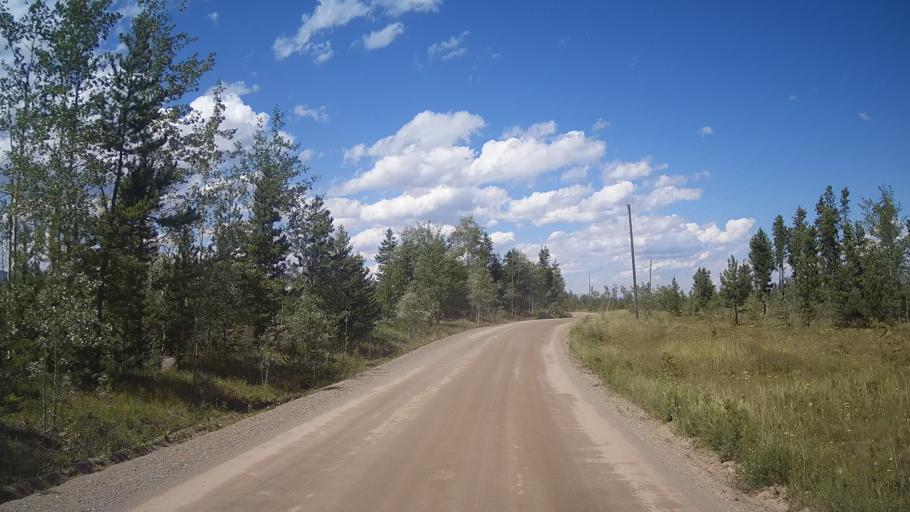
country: CA
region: British Columbia
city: Cache Creek
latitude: 51.2522
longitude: -121.6731
